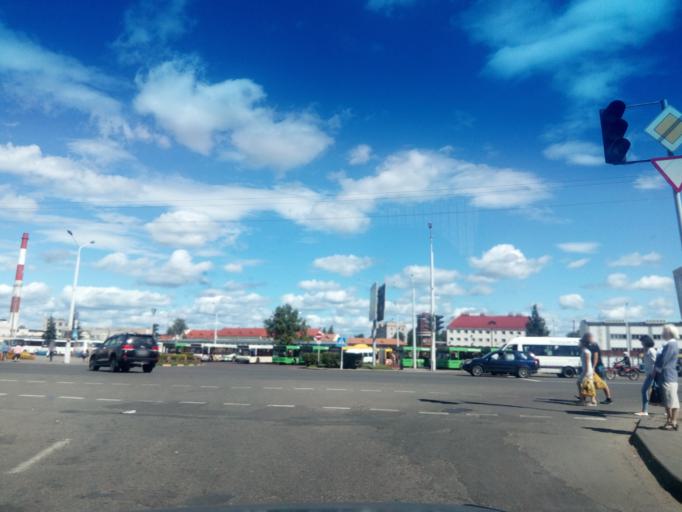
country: BY
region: Vitebsk
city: Polatsk
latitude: 55.4893
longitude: 28.7840
